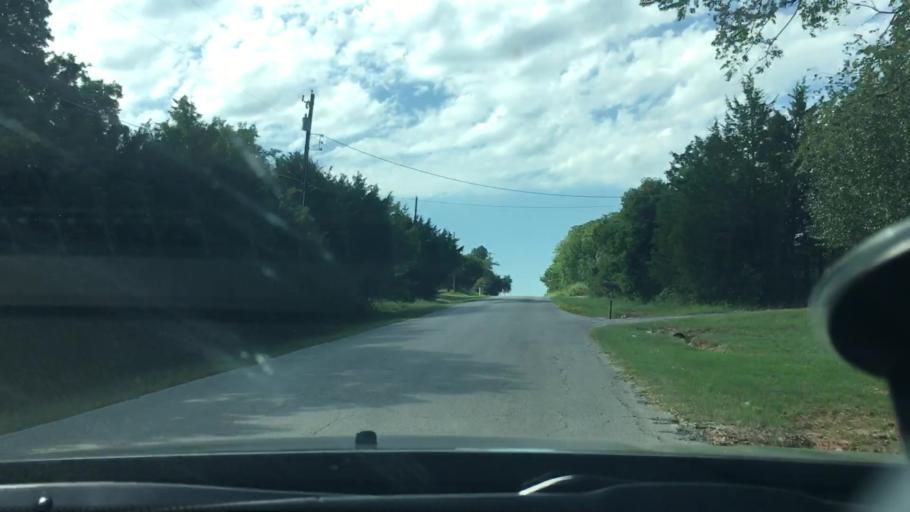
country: US
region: Oklahoma
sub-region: Carter County
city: Ardmore
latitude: 34.1546
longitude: -97.0906
